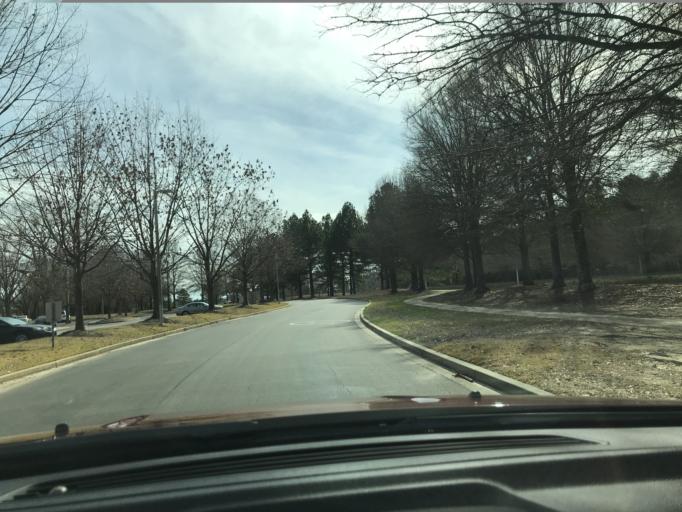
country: US
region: Tennessee
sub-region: Shelby County
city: Collierville
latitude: 35.0380
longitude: -89.7236
